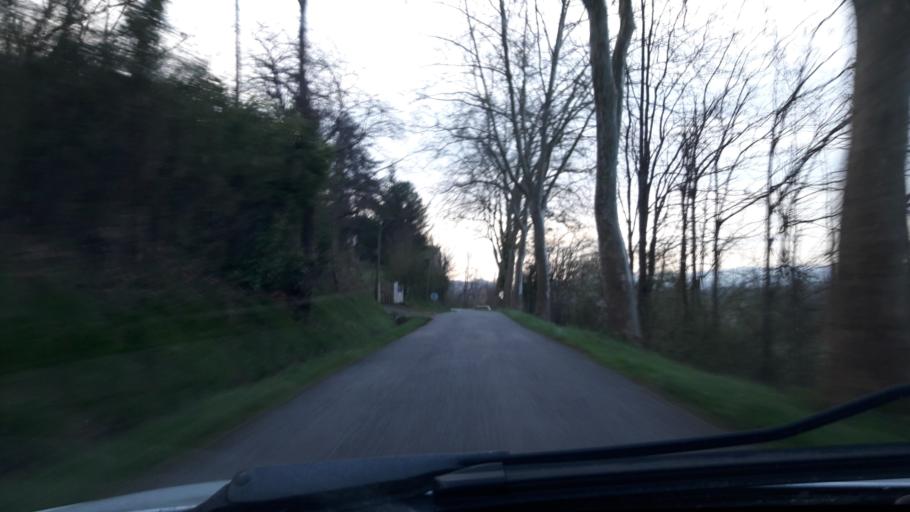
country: FR
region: Midi-Pyrenees
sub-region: Departement de la Haute-Garonne
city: Montesquieu-Volvestre
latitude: 43.2011
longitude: 1.2404
